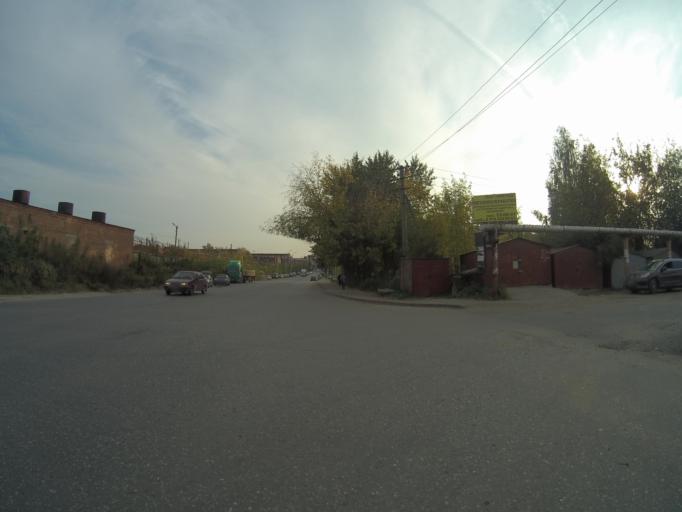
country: RU
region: Vladimir
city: Vladimir
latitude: 56.1542
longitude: 40.3812
